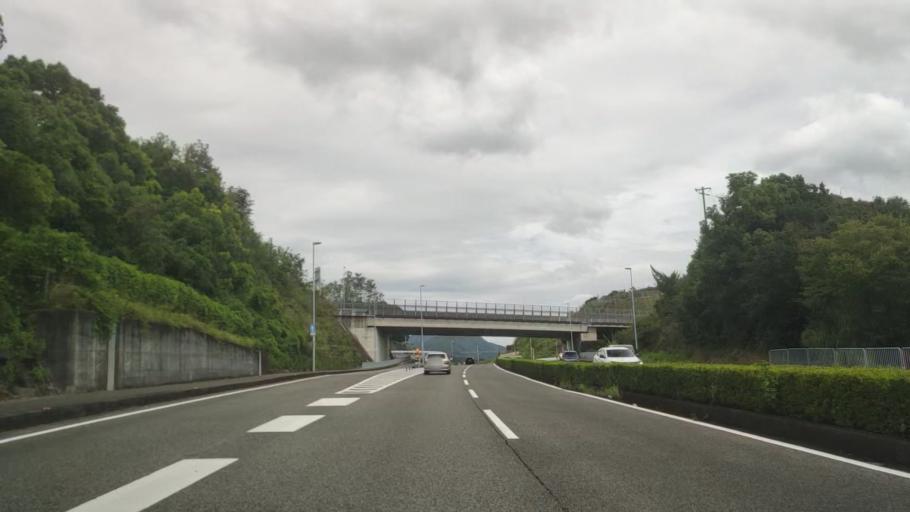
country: JP
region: Wakayama
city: Tanabe
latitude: 33.7313
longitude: 135.4004
